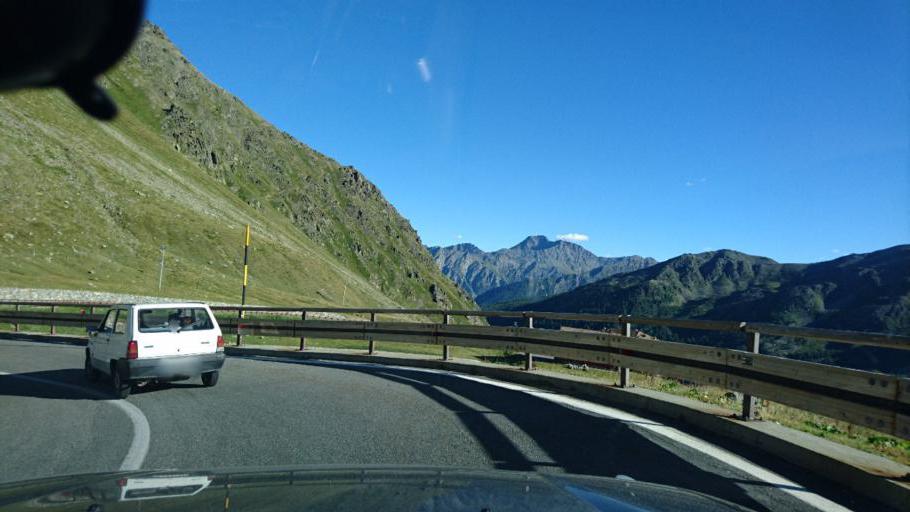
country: IT
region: Aosta Valley
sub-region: Valle d'Aosta
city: San Leonardo
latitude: 45.8632
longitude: 7.1601
